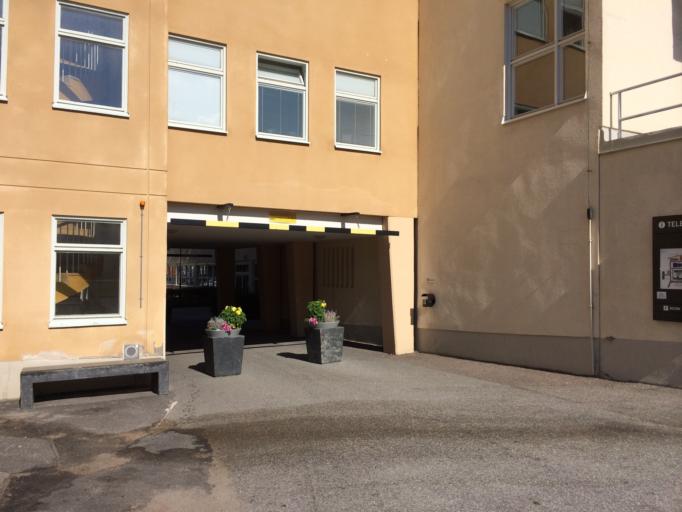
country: SE
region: Stockholm
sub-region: Stockholms Kommun
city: Arsta
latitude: 59.2981
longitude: 17.9927
